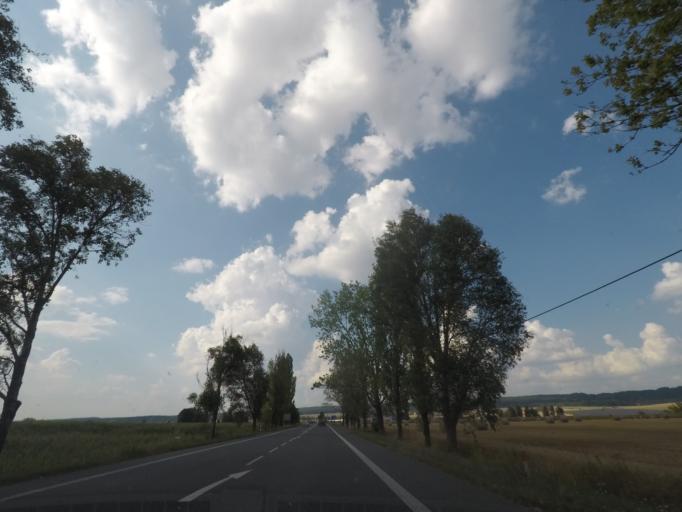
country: CZ
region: Kralovehradecky
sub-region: Okres Nachod
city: Jaromer
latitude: 50.4149
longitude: 15.8844
